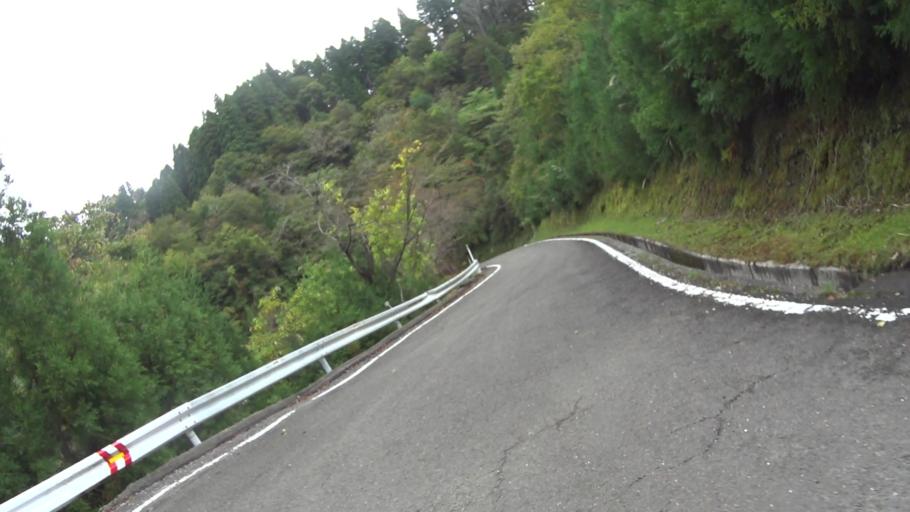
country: JP
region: Shiga Prefecture
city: Kitahama
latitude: 35.2744
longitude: 135.7259
